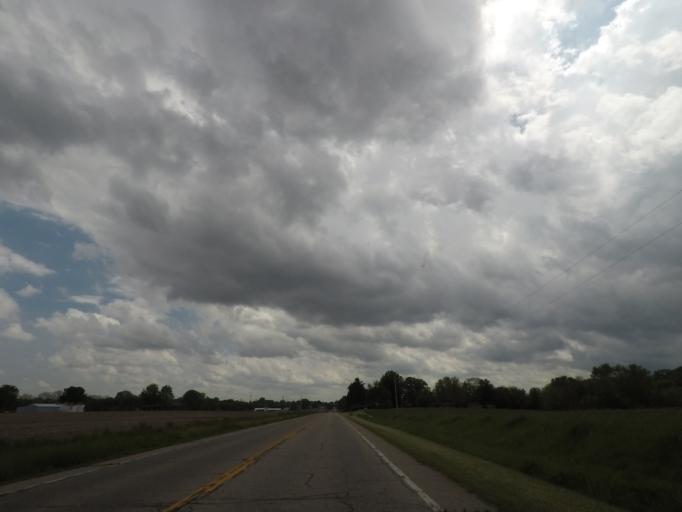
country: US
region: Illinois
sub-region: De Witt County
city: Clinton
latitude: 40.1685
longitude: -88.9605
